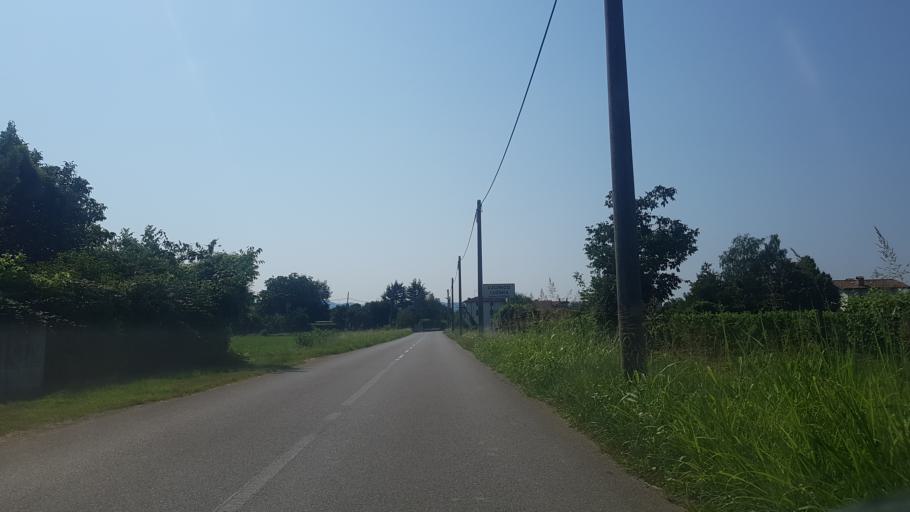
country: IT
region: Friuli Venezia Giulia
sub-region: Provincia di Gorizia
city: Mossa
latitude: 45.9430
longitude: 13.5734
